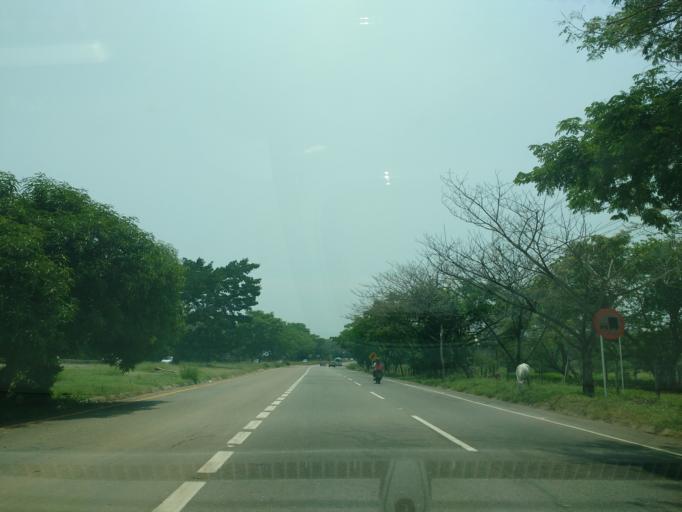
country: CO
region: Tolima
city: Melgar
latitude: 4.2132
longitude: -74.6743
